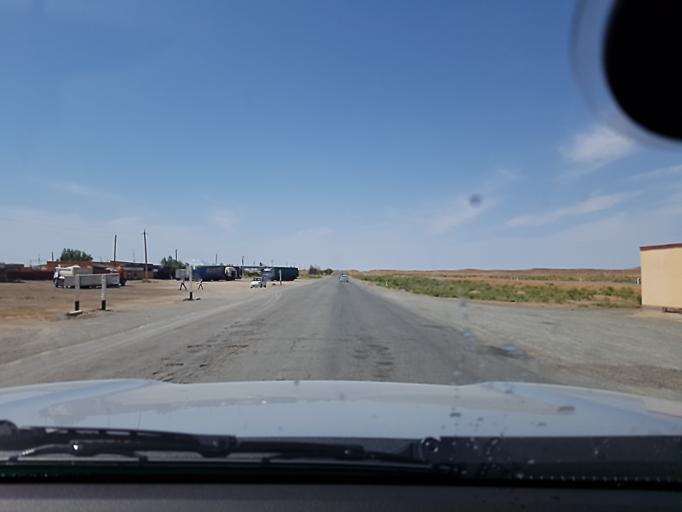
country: UZ
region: Karakalpakstan
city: Mang'it Shahri
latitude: 42.2451
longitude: 60.1521
